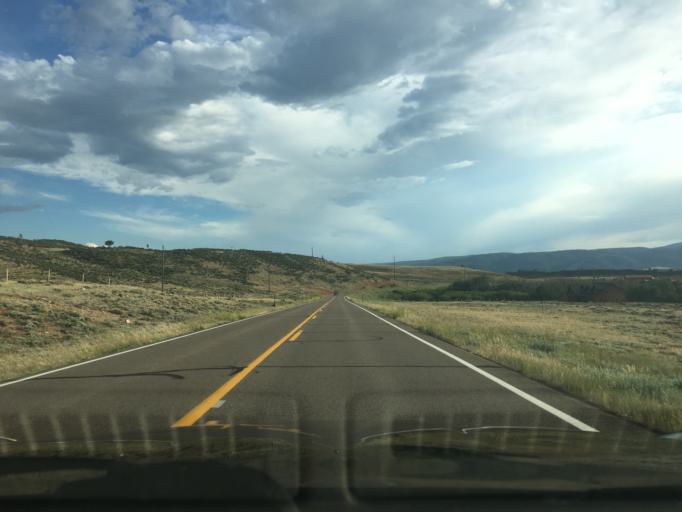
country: US
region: Wyoming
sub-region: Albany County
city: Laramie
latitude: 41.2757
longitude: -106.0682
